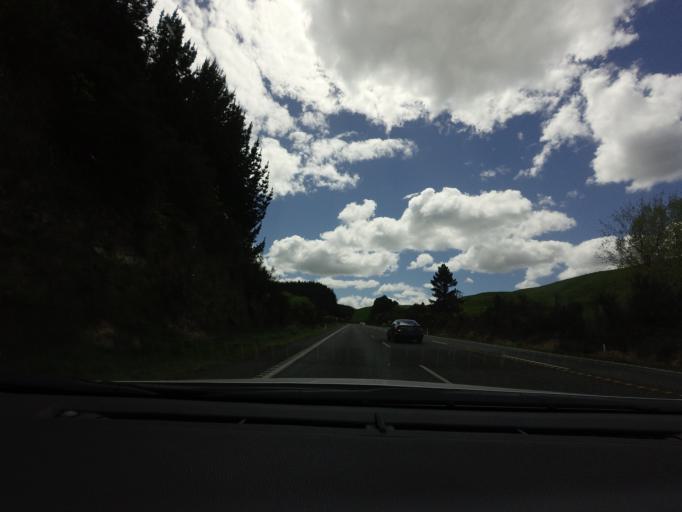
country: NZ
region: Bay of Plenty
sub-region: Rotorua District
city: Rotorua
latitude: -38.2914
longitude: 176.3533
